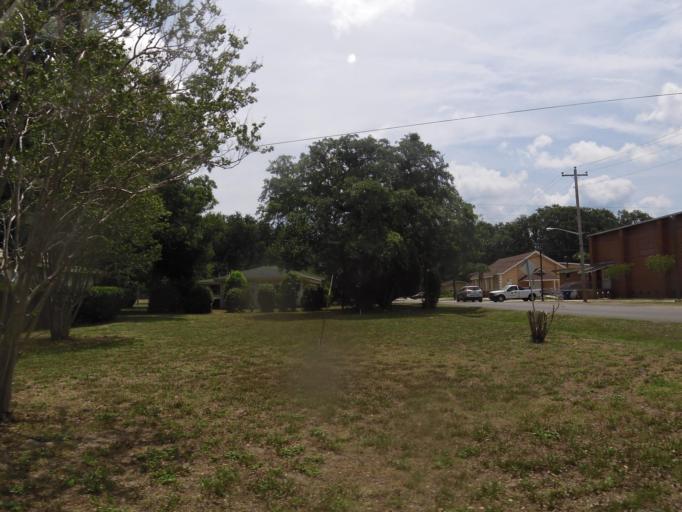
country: US
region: Florida
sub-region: Nassau County
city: Fernandina Beach
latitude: 30.6643
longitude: -81.4581
